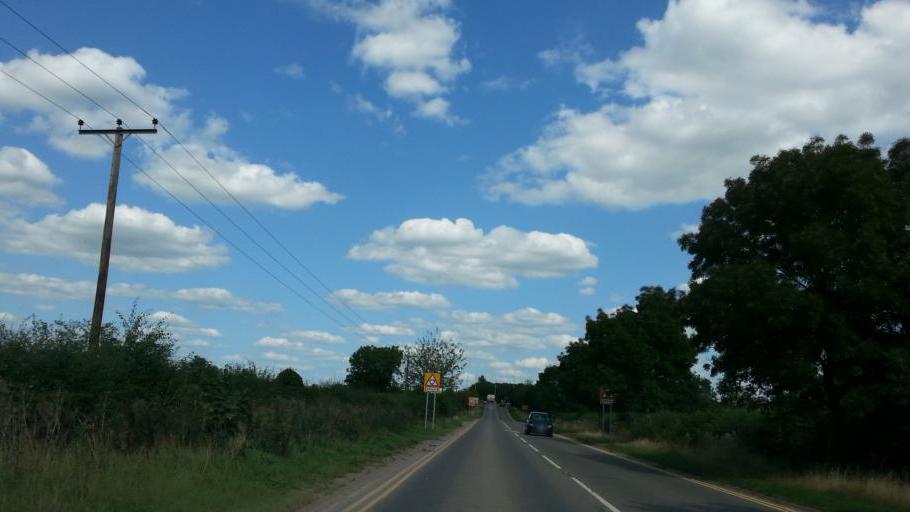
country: GB
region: England
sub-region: Leicestershire
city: Barrow upon Soar
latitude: 52.7385
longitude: -1.1485
